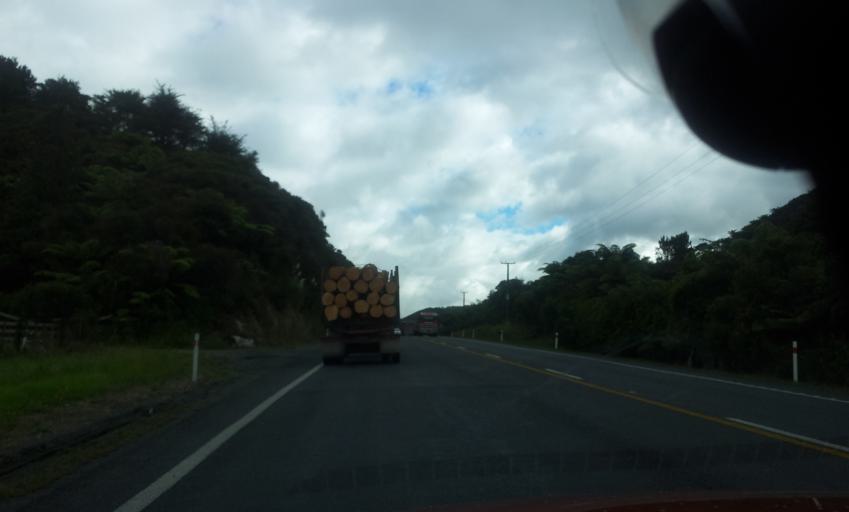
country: NZ
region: Auckland
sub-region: Auckland
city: Wellsford
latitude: -36.1163
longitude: 174.4352
